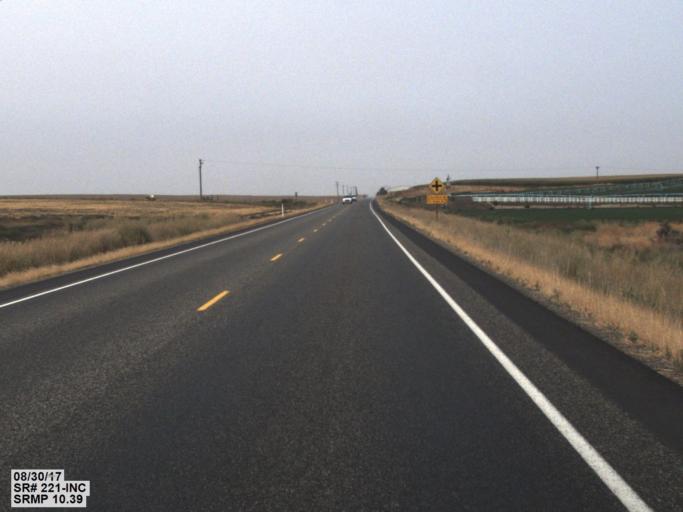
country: US
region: Washington
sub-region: Benton County
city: Prosser
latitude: 46.0856
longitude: -119.6021
